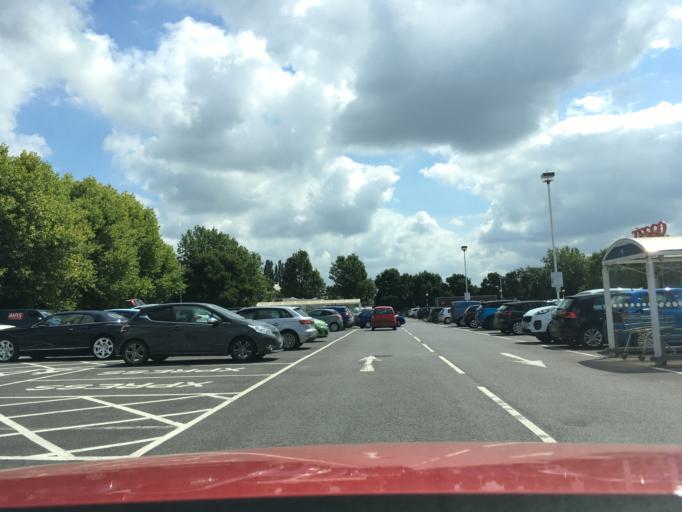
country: GB
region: England
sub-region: Gloucestershire
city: Gloucester
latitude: 51.8720
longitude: -2.2496
